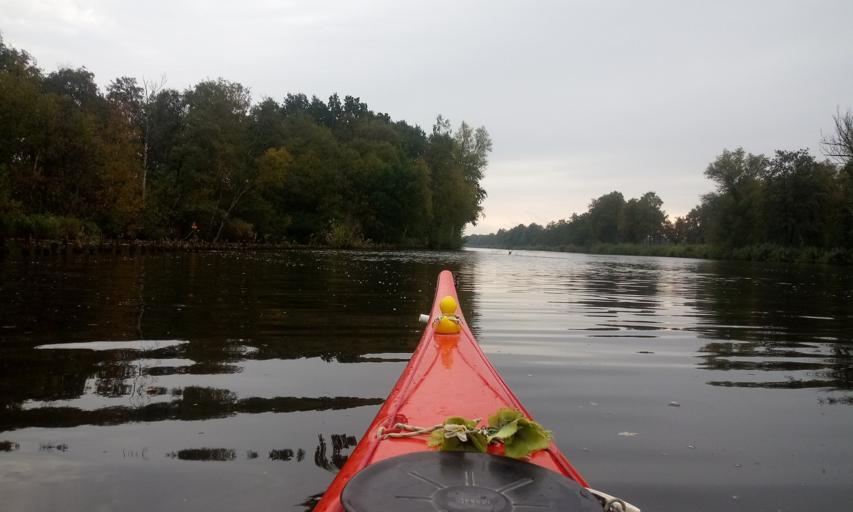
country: NL
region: North Holland
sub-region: Gemeente Wijdemeren
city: Kortenhoef
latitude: 52.2244
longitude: 5.0926
